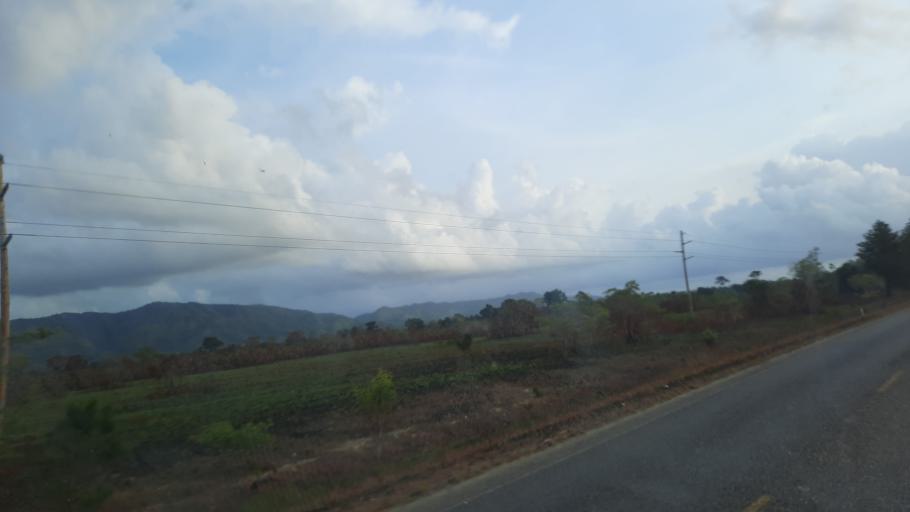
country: BZ
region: Stann Creek
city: Placencia
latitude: 16.6919
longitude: -88.4358
